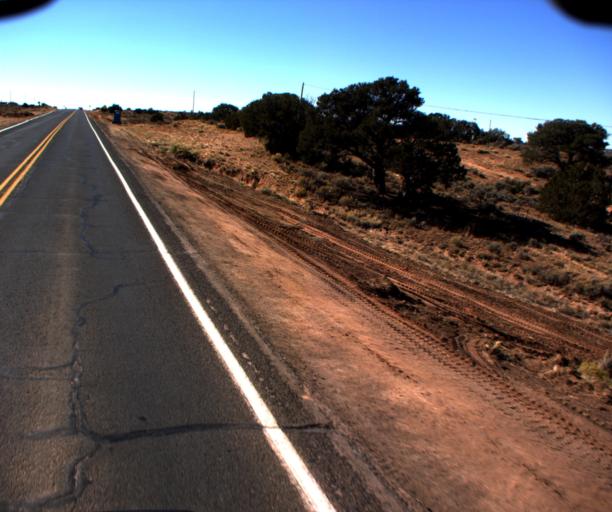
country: US
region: Arizona
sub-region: Apache County
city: Ganado
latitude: 35.7111
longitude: -109.5074
